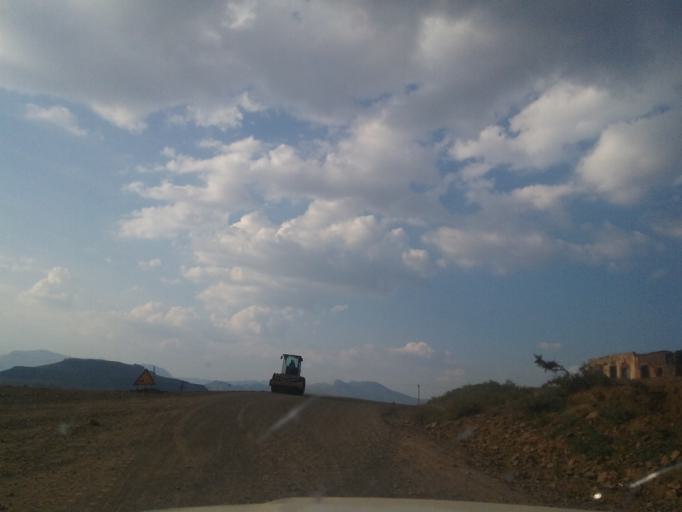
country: LS
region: Quthing
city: Quthing
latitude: -30.4086
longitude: 27.6054
